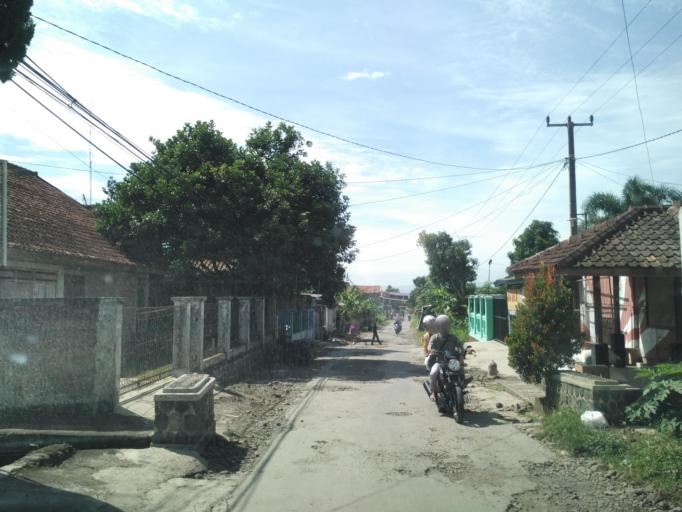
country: ID
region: West Java
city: Ciranjang-hilir
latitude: -6.8448
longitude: 107.1166
